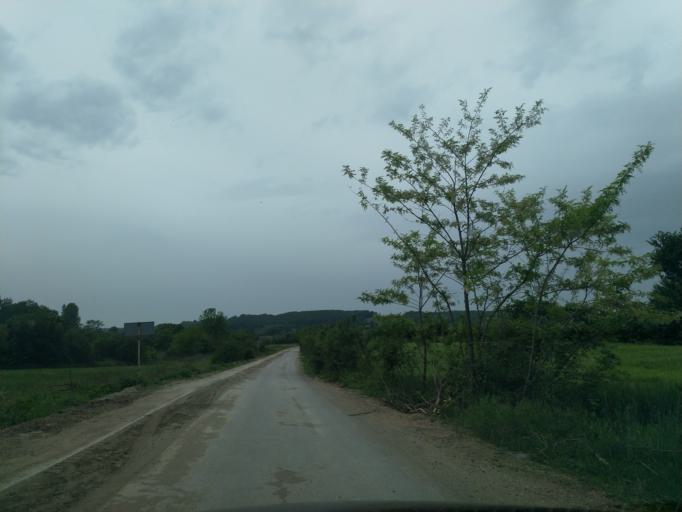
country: RS
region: Central Serbia
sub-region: Pomoravski Okrug
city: Paracin
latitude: 43.8658
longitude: 21.5779
